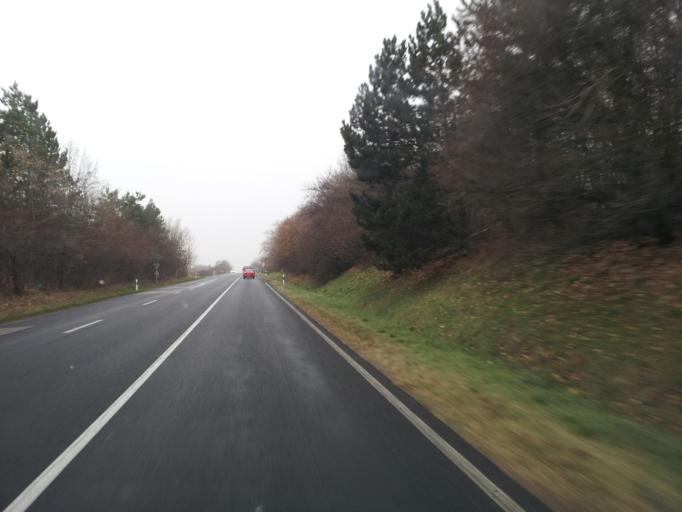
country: HU
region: Veszprem
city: Ajka
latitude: 47.1402
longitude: 17.5917
